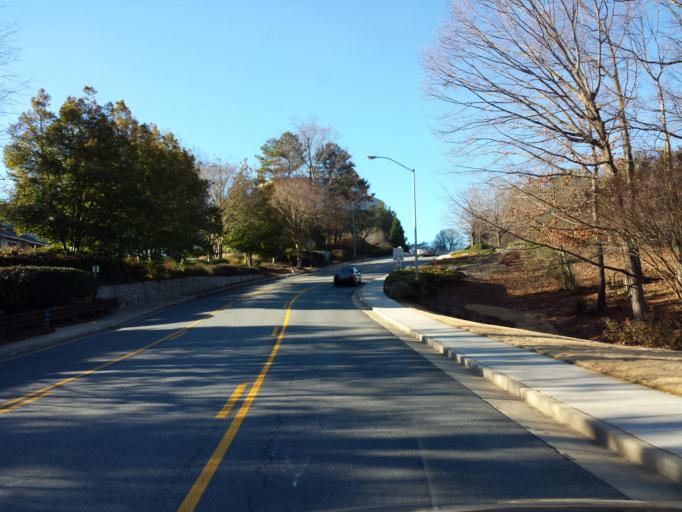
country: US
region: Georgia
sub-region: Cobb County
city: Vinings
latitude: 33.8998
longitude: -84.4592
